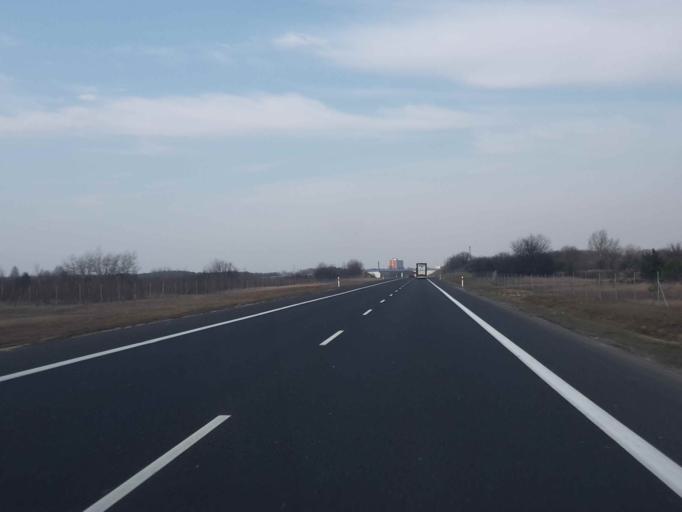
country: PL
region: Kujawsko-Pomorskie
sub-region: Torun
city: Torun
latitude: 52.9831
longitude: 18.5998
